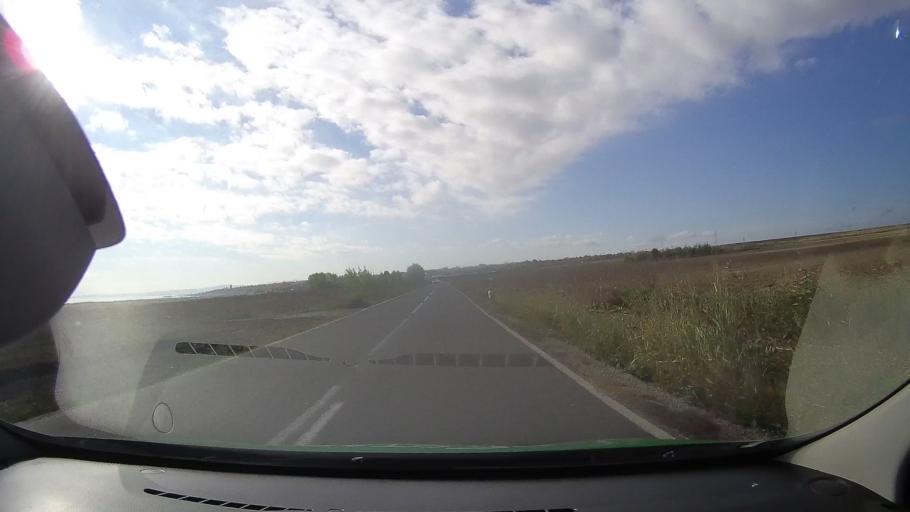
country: RO
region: Tulcea
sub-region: Comuna Sarichioi
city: Sarichioi
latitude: 44.9618
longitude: 28.8605
